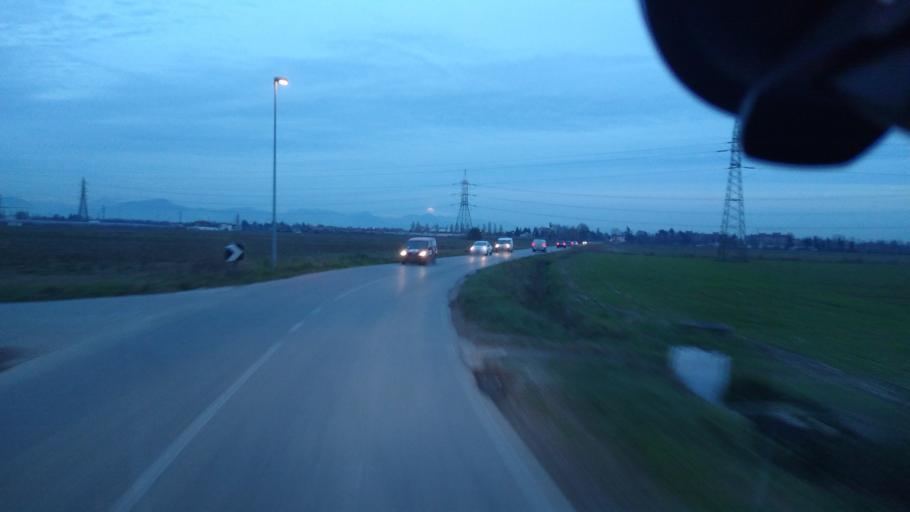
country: IT
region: Lombardy
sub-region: Provincia di Bergamo
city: Ciserano
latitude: 45.5722
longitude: 9.5970
